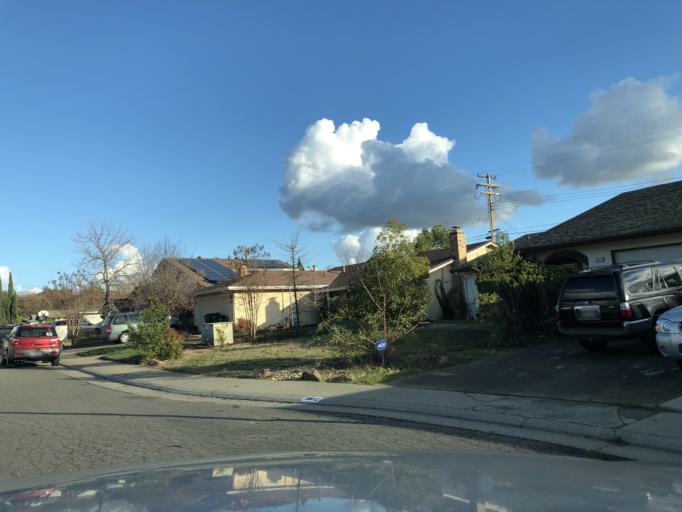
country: US
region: California
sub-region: Sacramento County
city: Foothill Farms
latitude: 38.6549
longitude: -121.3303
